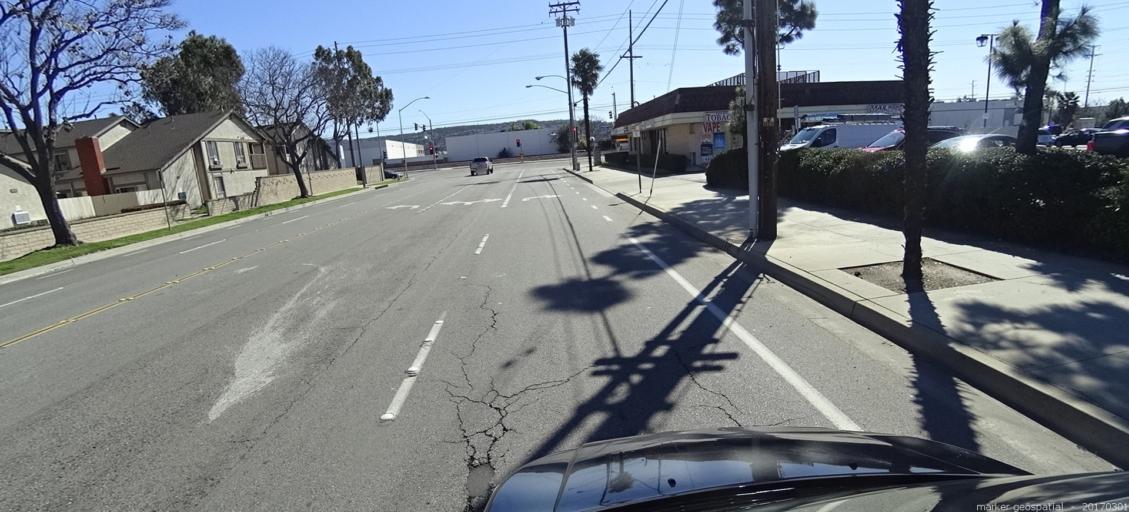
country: US
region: California
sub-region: Orange County
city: Yorba Linda
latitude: 33.8656
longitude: -117.8045
